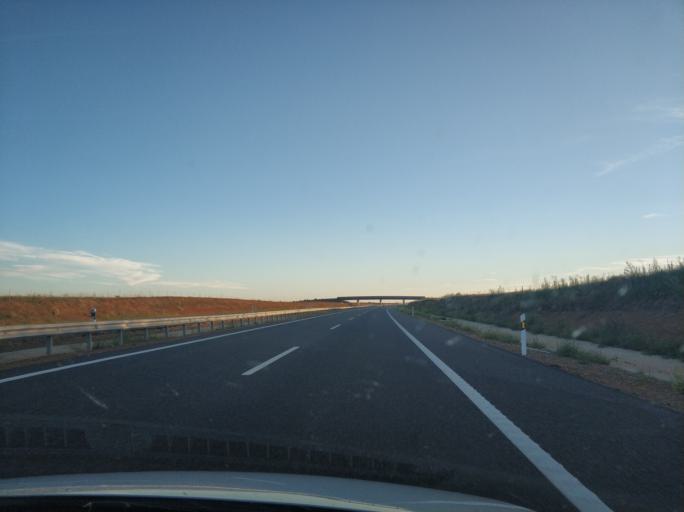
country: ES
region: Castille and Leon
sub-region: Provincia de Zamora
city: Castrogonzalo
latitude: 41.9560
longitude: -5.6168
